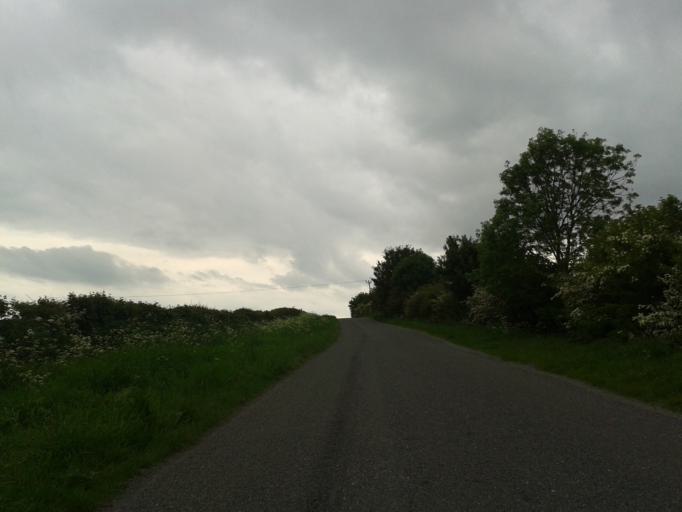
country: GB
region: England
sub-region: Cambridgeshire
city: Sawtry
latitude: 52.4020
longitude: -0.3123
